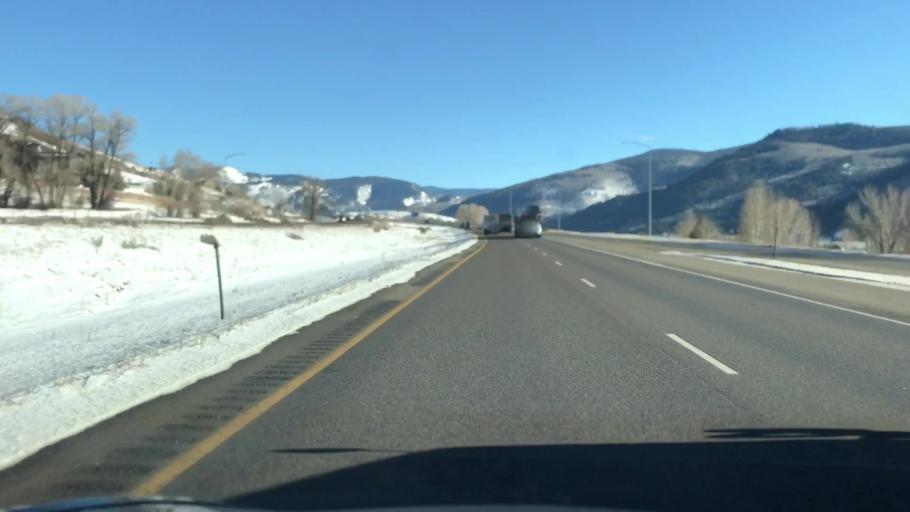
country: US
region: Colorado
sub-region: Eagle County
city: Avon
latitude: 39.6357
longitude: -106.5189
